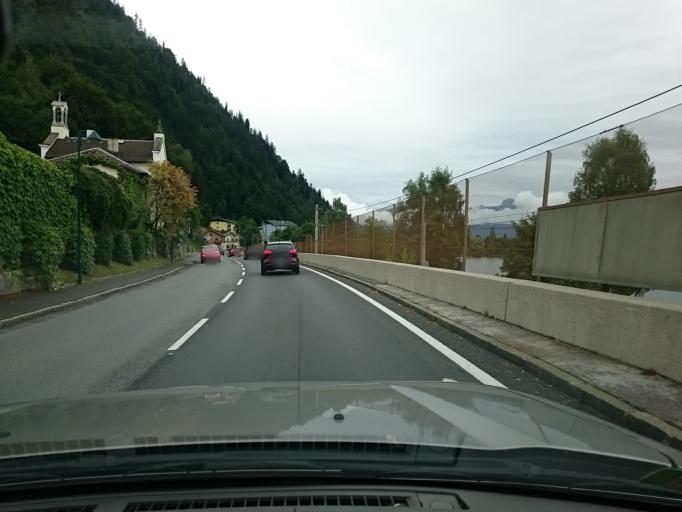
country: AT
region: Salzburg
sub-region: Politischer Bezirk Zell am See
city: Zell am See
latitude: 47.3353
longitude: 12.7977
